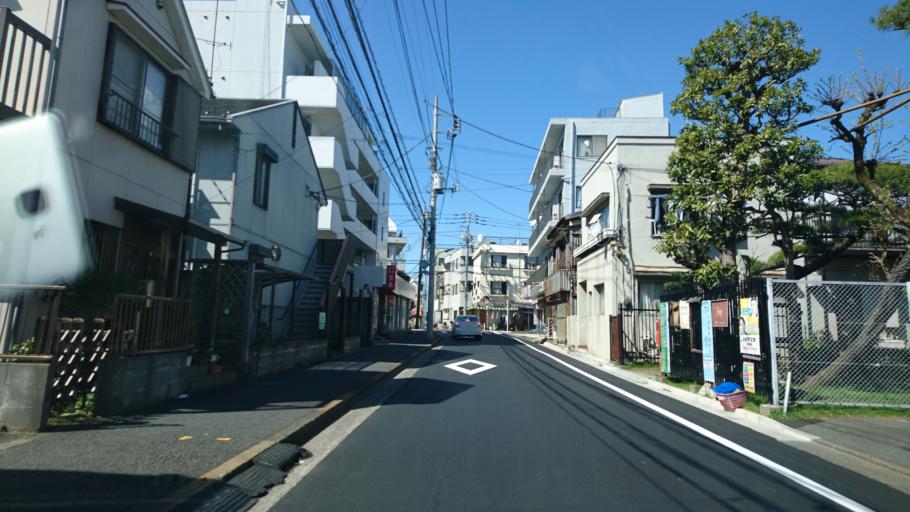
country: JP
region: Kanagawa
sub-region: Kawasaki-shi
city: Kawasaki
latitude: 35.5760
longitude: 139.7118
